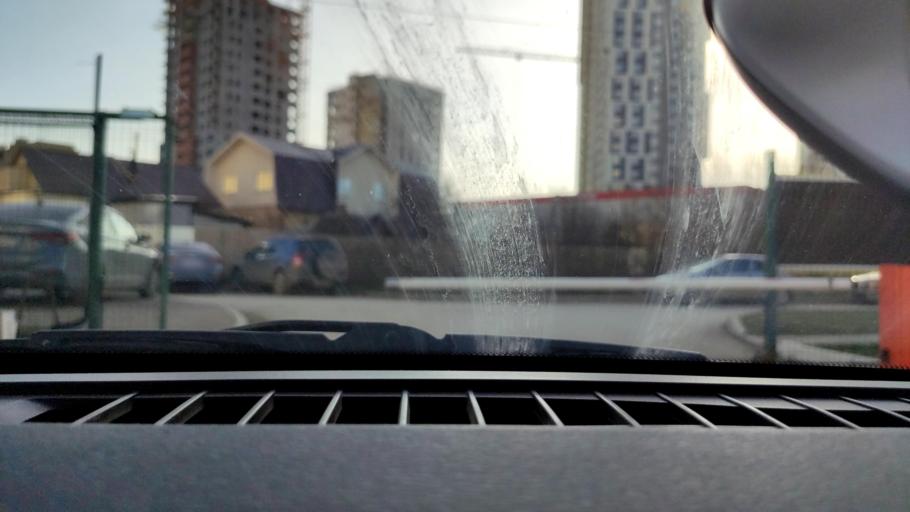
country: RU
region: Perm
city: Perm
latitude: 57.9751
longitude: 56.1866
